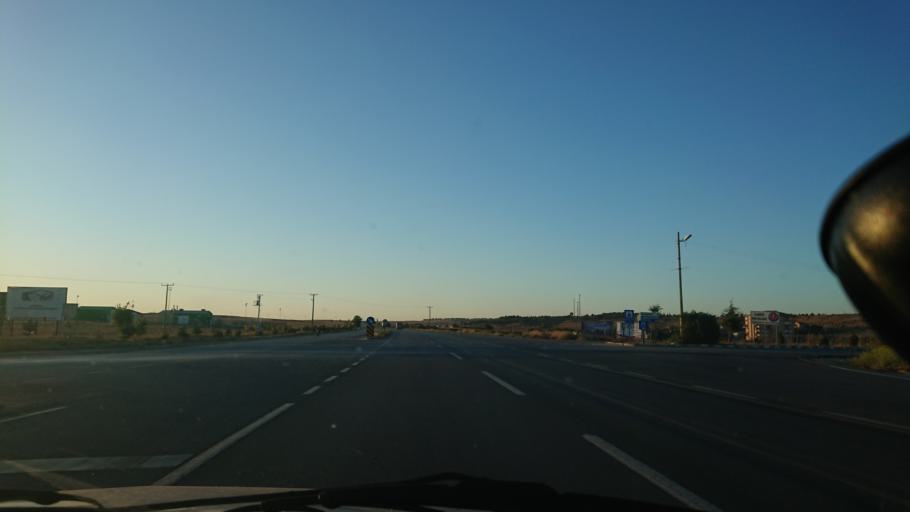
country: TR
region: Eskisehir
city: Mahmudiye
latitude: 39.4878
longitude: 30.9827
